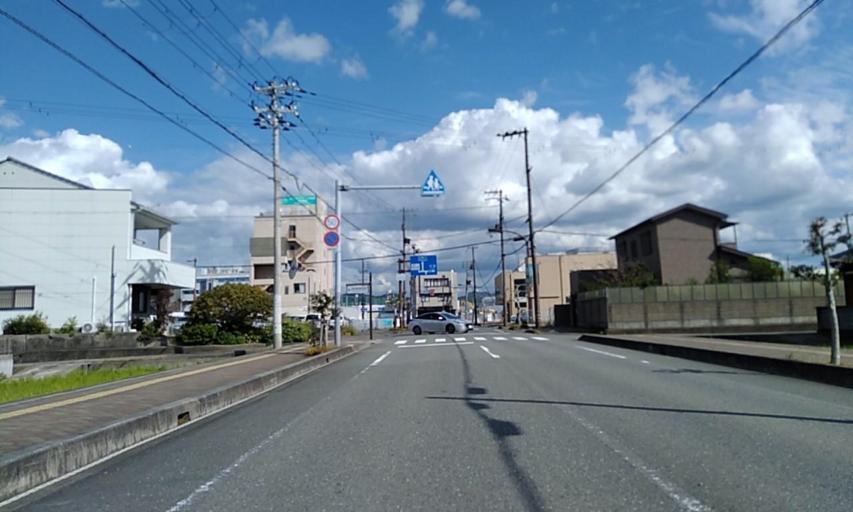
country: JP
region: Wakayama
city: Gobo
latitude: 33.9066
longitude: 135.1584
